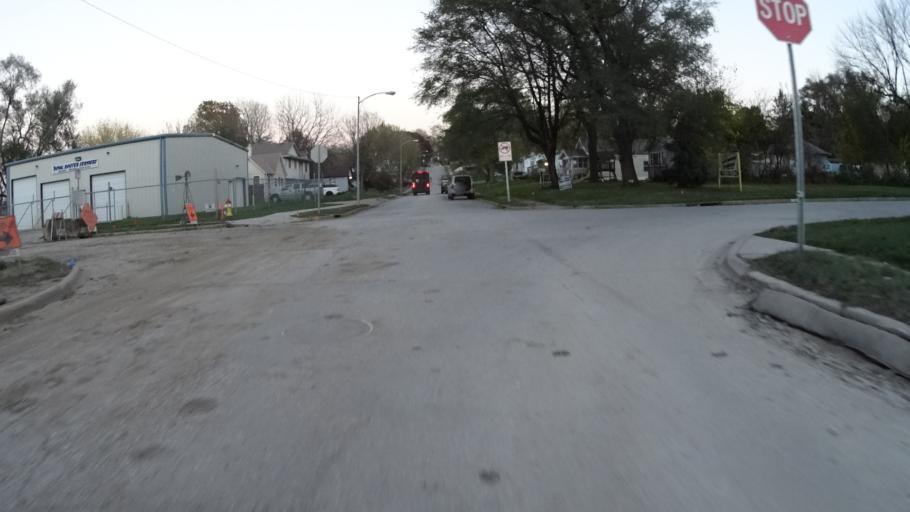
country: US
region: Nebraska
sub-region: Douglas County
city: Omaha
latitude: 41.1918
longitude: -95.9482
